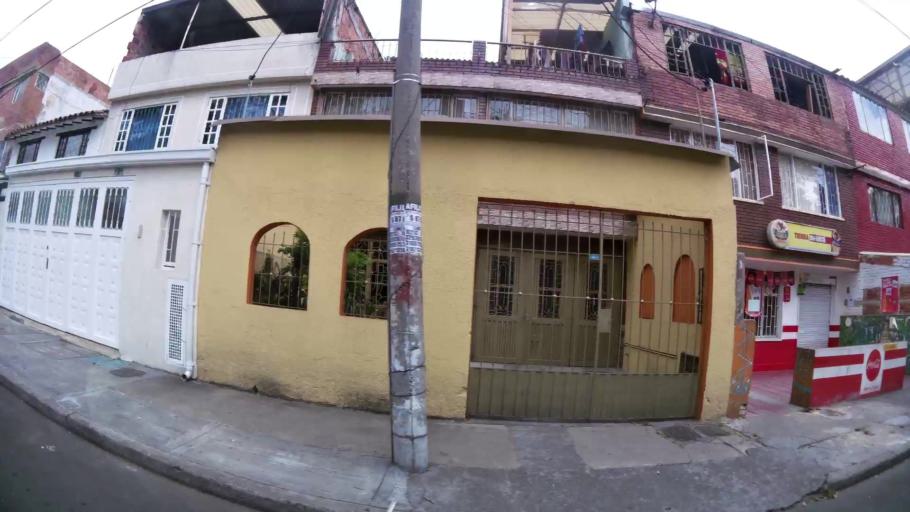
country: CO
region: Bogota D.C.
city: Bogota
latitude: 4.6241
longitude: -74.1083
